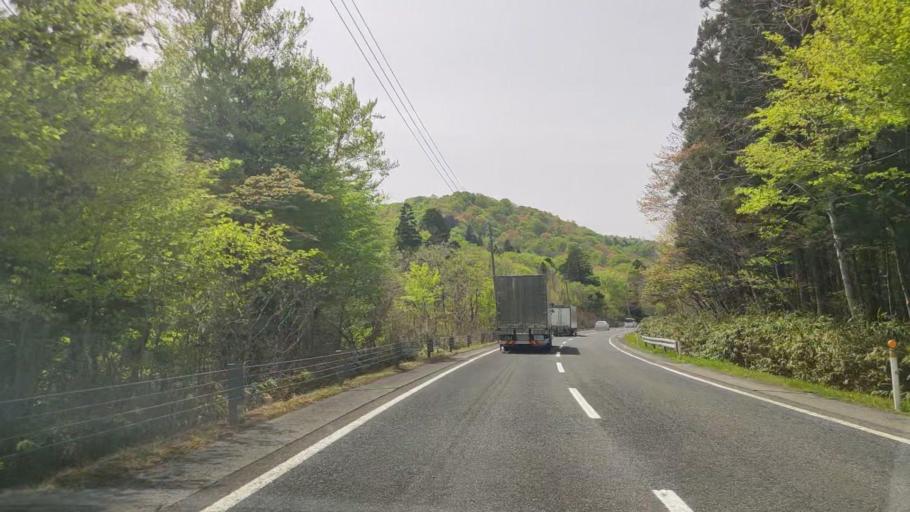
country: JP
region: Aomori
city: Aomori Shi
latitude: 40.7758
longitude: 141.0225
